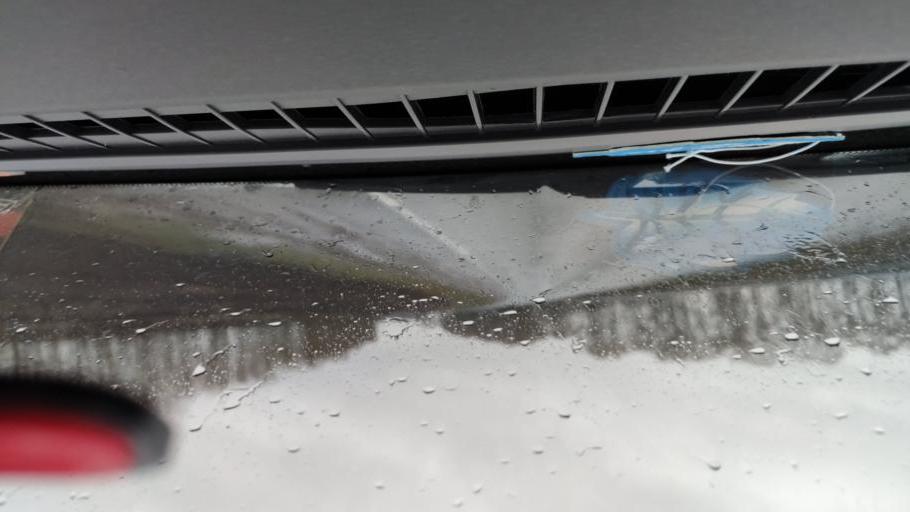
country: RU
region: Tatarstan
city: Mendeleyevsk
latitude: 55.8477
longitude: 52.2082
